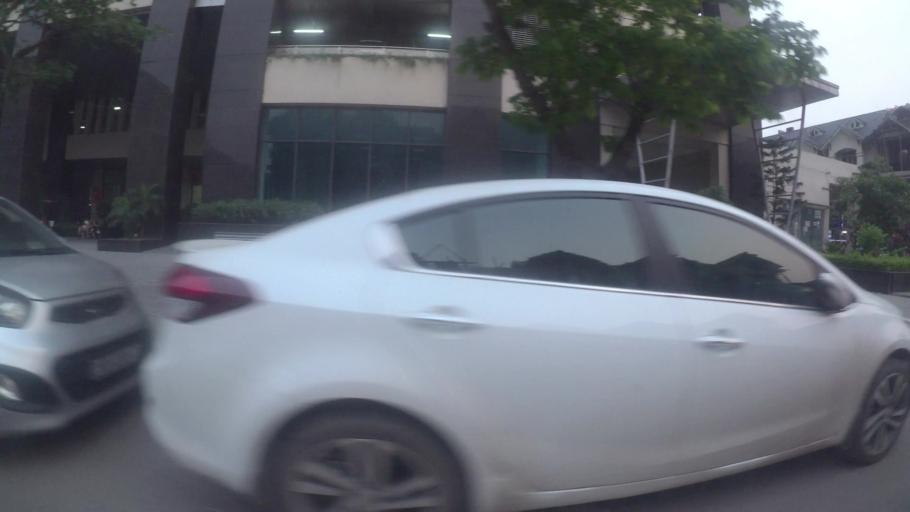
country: VN
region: Ha Noi
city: Cau Dien
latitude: 21.0034
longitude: 105.7316
